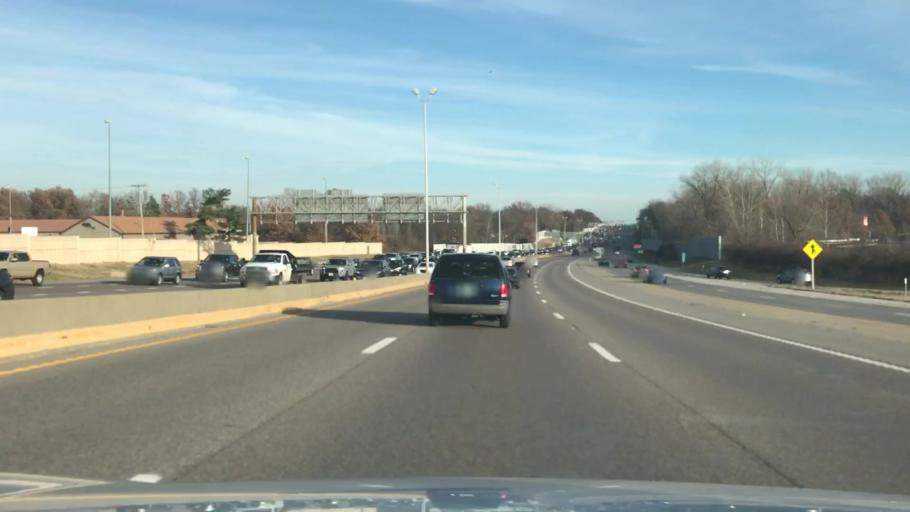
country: US
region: Missouri
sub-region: Saint Louis County
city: Frontenac
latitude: 38.6393
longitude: -90.4420
